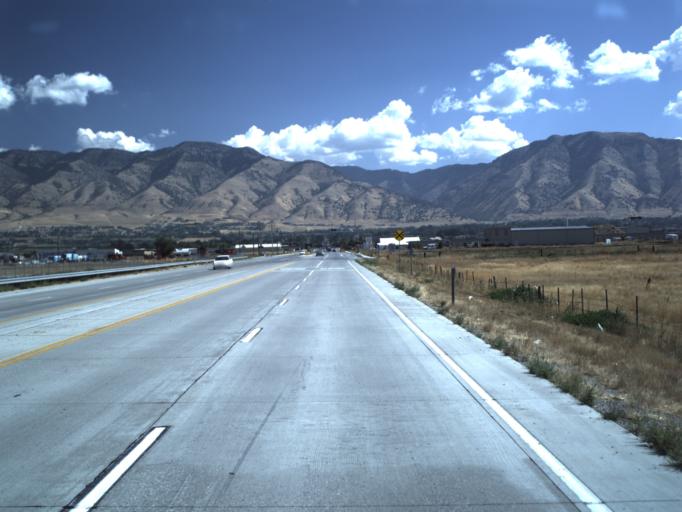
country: US
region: Utah
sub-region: Cache County
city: Hyde Park
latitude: 41.7779
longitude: -111.8506
